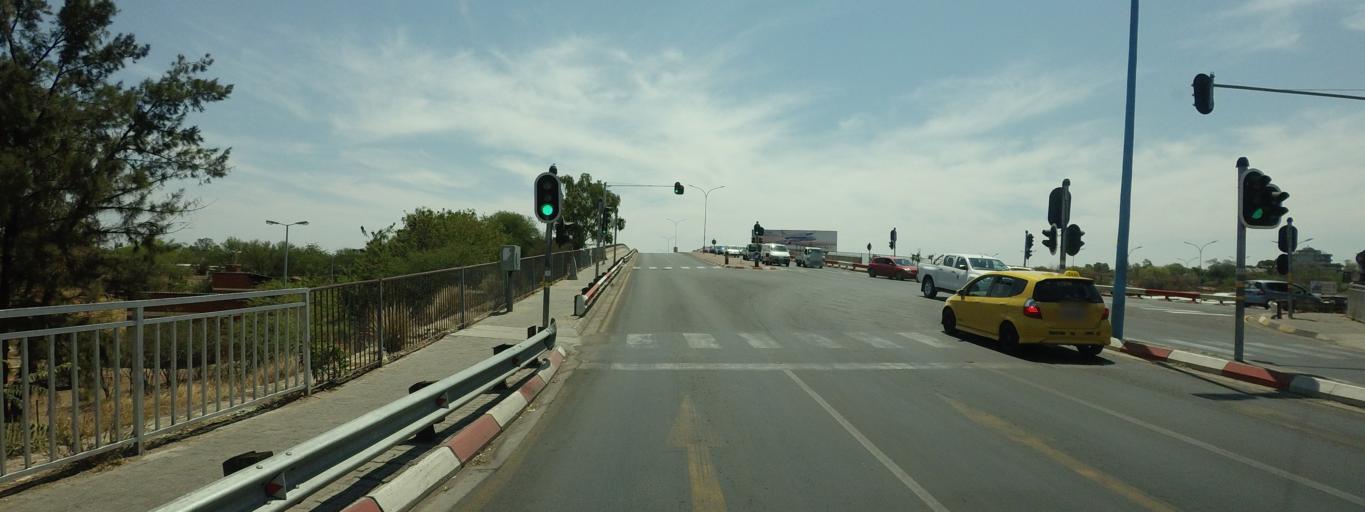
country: BW
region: North East
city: Francistown
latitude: -21.1733
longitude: 27.5108
